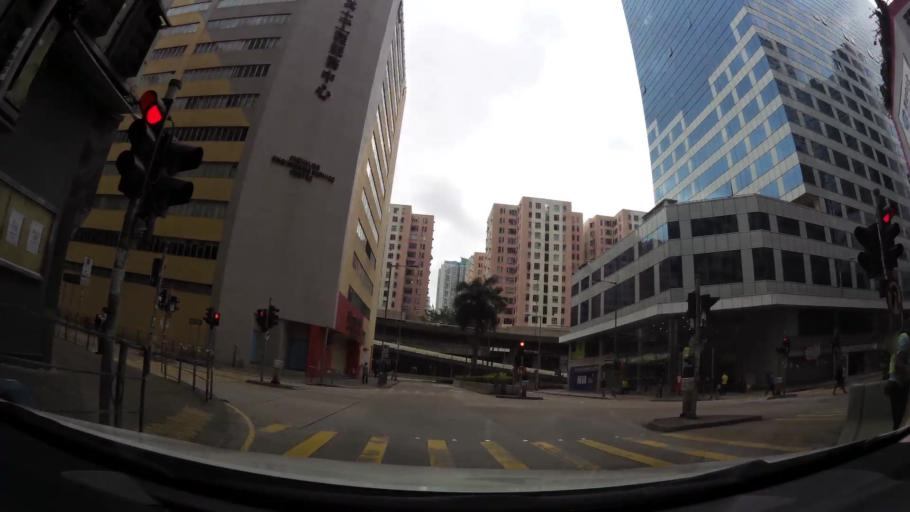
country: HK
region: Kowloon City
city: Kowloon
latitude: 22.3219
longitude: 114.2108
